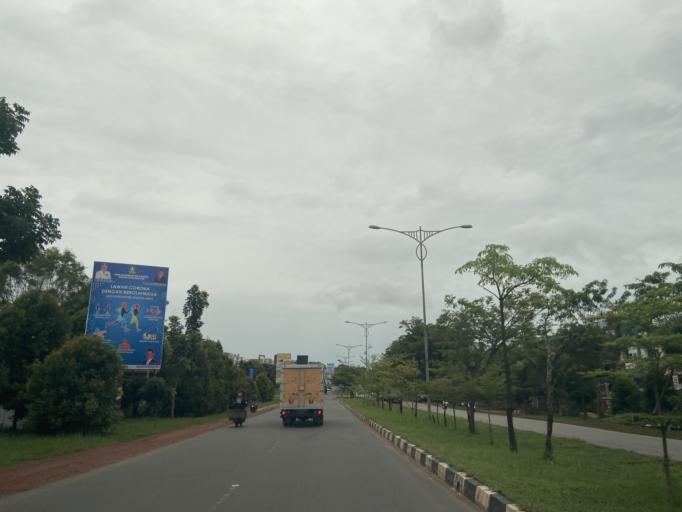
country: SG
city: Singapore
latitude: 1.1191
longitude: 104.0582
